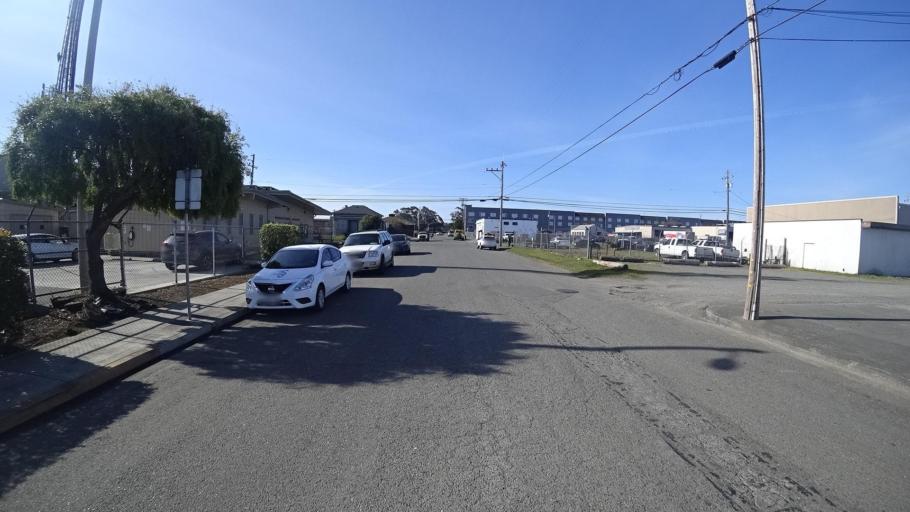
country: US
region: California
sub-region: Humboldt County
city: Eureka
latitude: 40.8068
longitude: -124.1493
